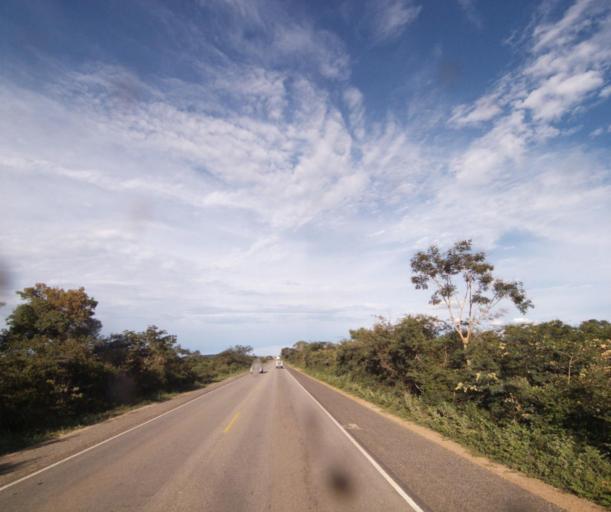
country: BR
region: Bahia
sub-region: Caetite
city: Caetite
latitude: -14.0783
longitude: -42.5521
